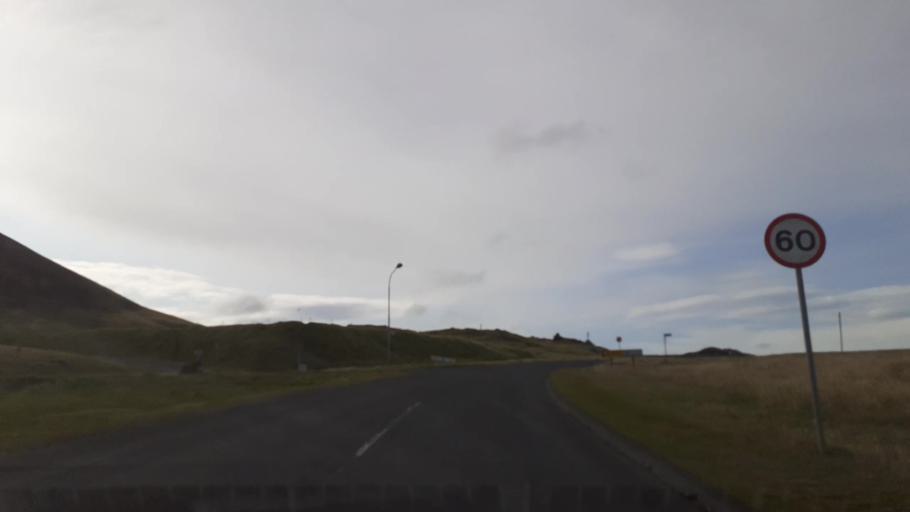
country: IS
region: South
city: Vestmannaeyjar
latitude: 63.4324
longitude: -20.2708
